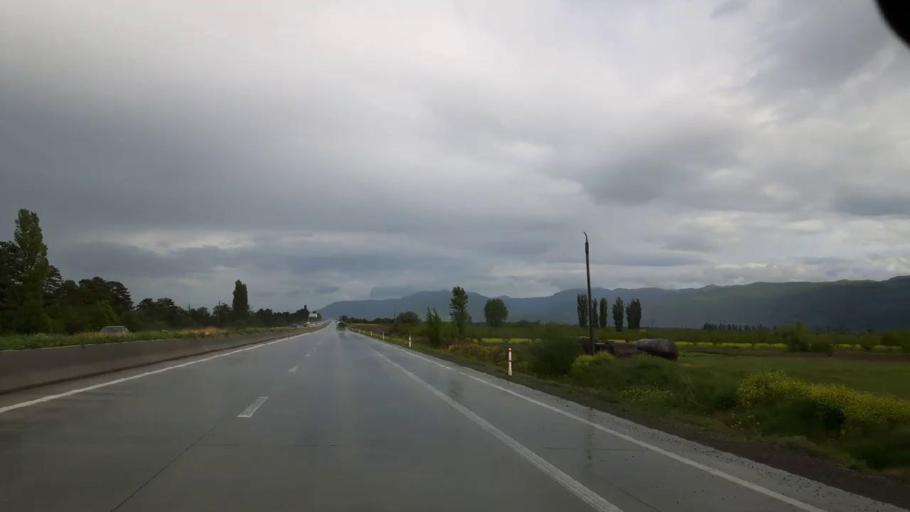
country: GE
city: Agara
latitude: 42.0440
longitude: 43.9231
